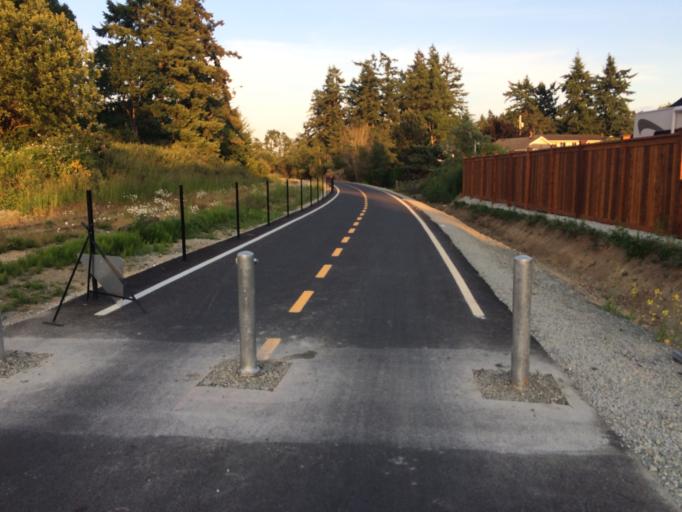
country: CA
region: British Columbia
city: Colwood
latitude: 48.4598
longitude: -123.4424
